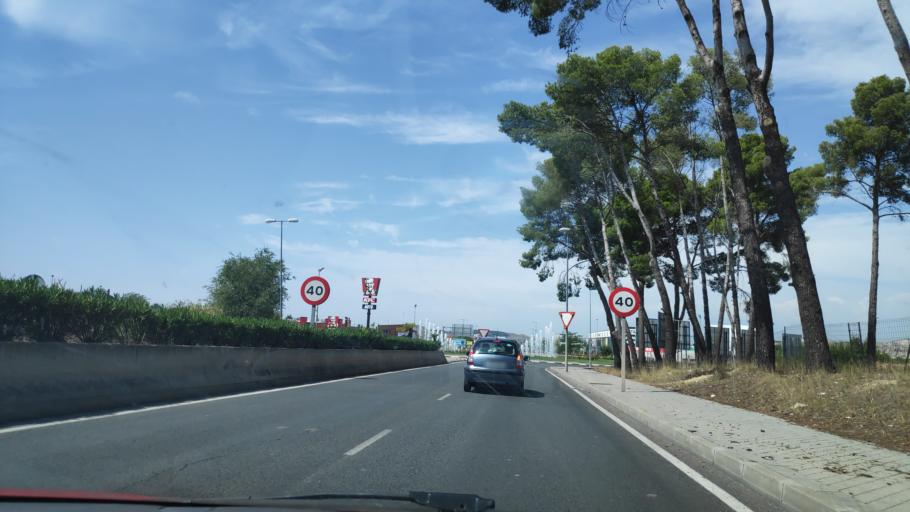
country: ES
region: Madrid
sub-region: Provincia de Madrid
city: Arganda
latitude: 40.3085
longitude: -3.4737
